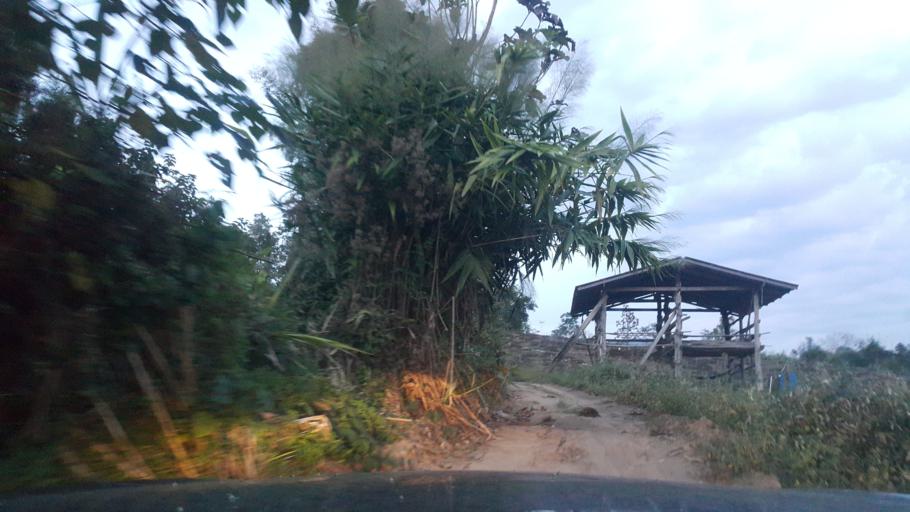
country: TH
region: Chiang Mai
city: Samoeng
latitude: 18.9467
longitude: 98.6720
